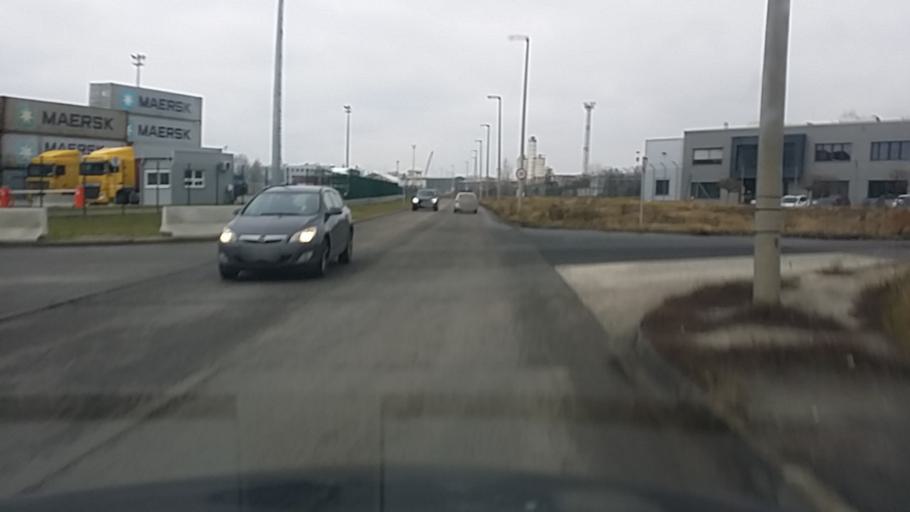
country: HU
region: Budapest
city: Budapest XXII. keruelet
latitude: 47.4173
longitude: 19.0520
